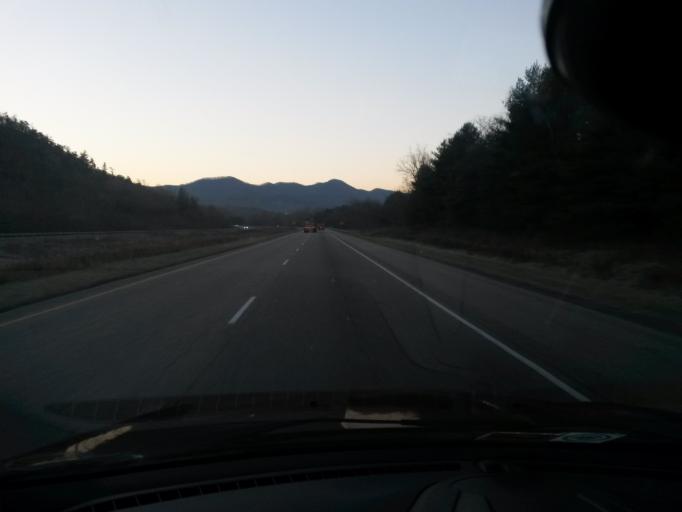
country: US
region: Virginia
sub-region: Alleghany County
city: Clifton Forge
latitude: 37.8125
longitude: -79.7410
